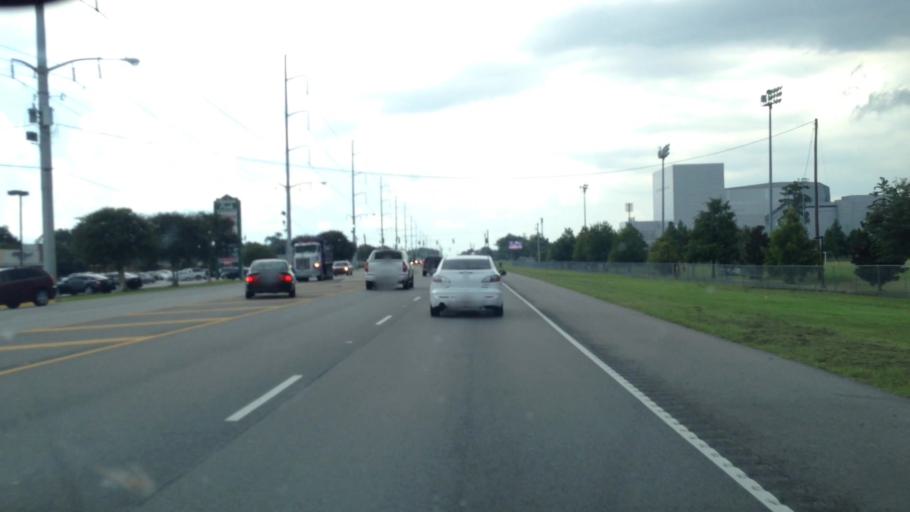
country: US
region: Louisiana
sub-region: Jefferson Parish
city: River Ridge
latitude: 29.9775
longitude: -90.2068
